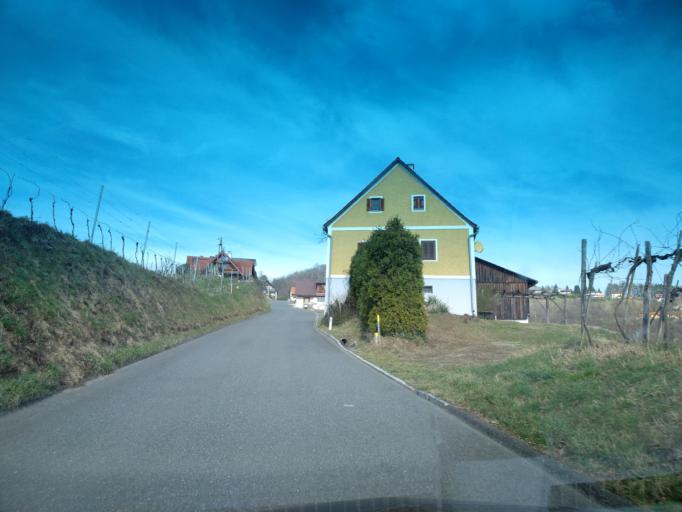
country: AT
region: Styria
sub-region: Politischer Bezirk Leibnitz
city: Kitzeck im Sausal
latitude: 46.7721
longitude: 15.4535
